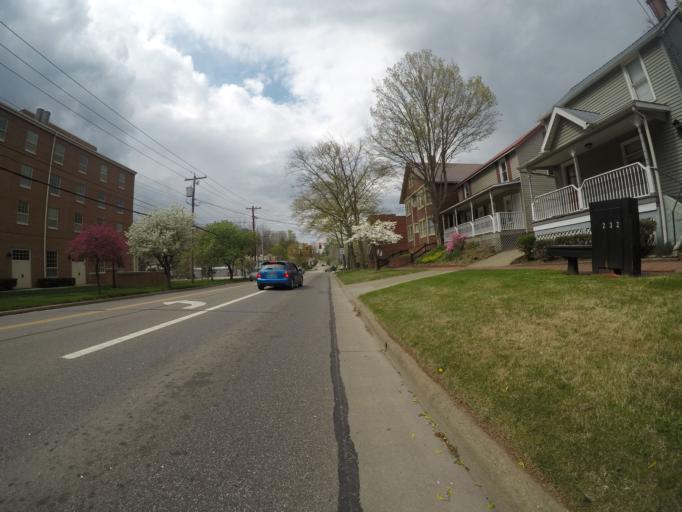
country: US
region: Ohio
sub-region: Washington County
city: Marietta
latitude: 39.4189
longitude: -81.4477
